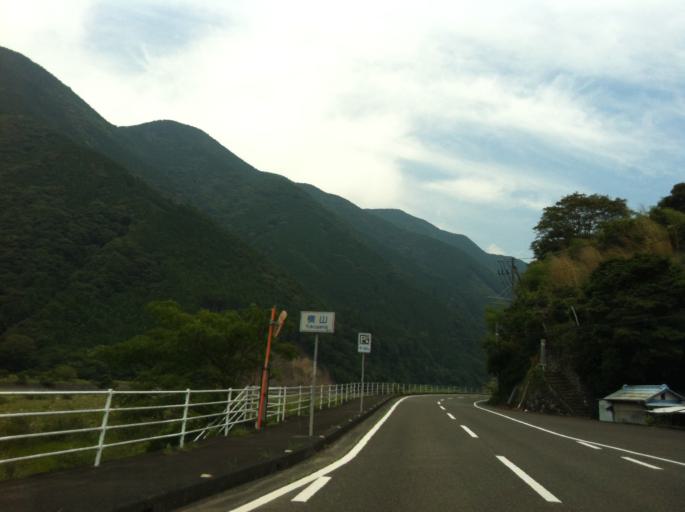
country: JP
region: Shizuoka
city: Shizuoka-shi
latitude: 35.1357
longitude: 138.3653
